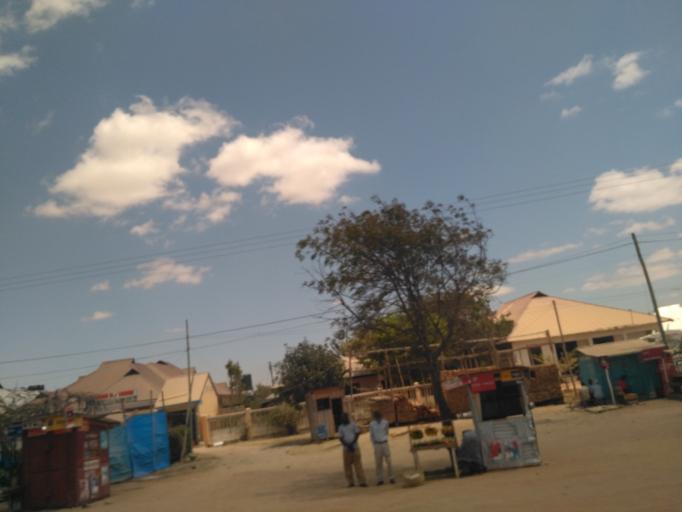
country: TZ
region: Dodoma
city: Kisasa
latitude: -6.1641
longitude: 35.7878
